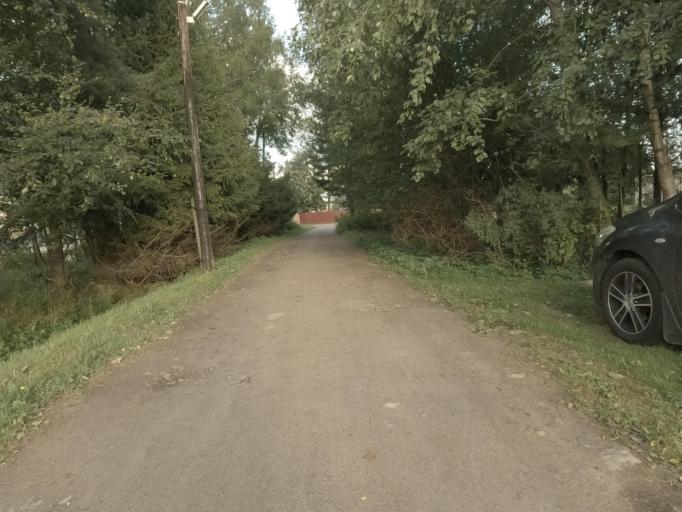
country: RU
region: Leningrad
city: Mga
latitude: 59.7521
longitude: 31.0336
